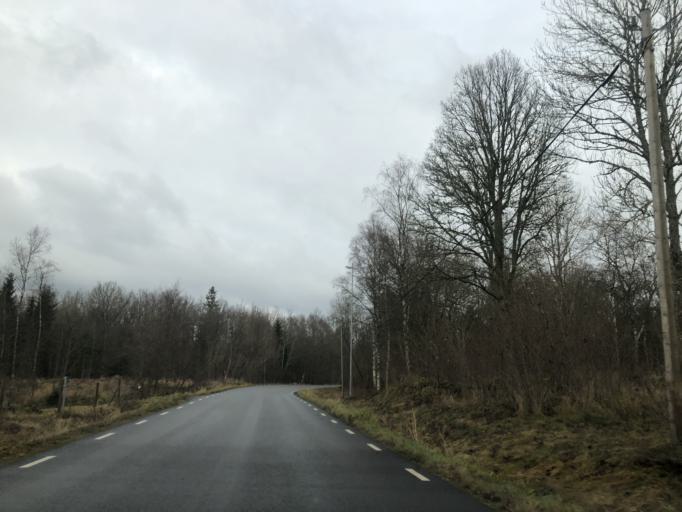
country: SE
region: Vaestra Goetaland
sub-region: Ulricehamns Kommun
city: Ulricehamn
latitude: 57.8316
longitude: 13.2585
